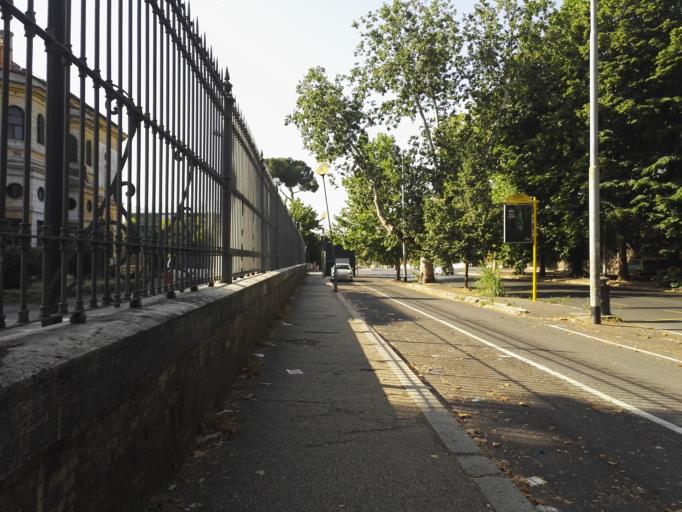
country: IT
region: Latium
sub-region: Citta metropolitana di Roma Capitale
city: Rome
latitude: 41.9048
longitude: 12.5106
